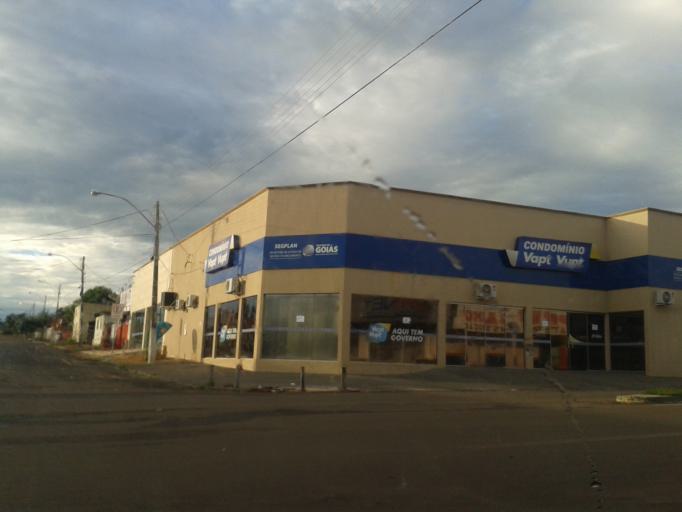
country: BR
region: Goias
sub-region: Sao Miguel Do Araguaia
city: Sao Miguel do Araguaia
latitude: -13.2708
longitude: -50.1607
